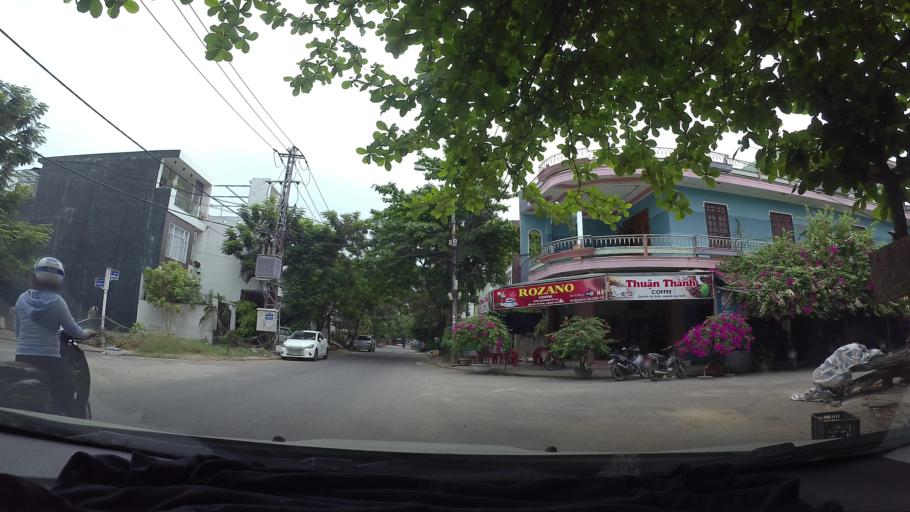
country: VN
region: Da Nang
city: Lien Chieu
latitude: 16.0726
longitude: 108.1680
